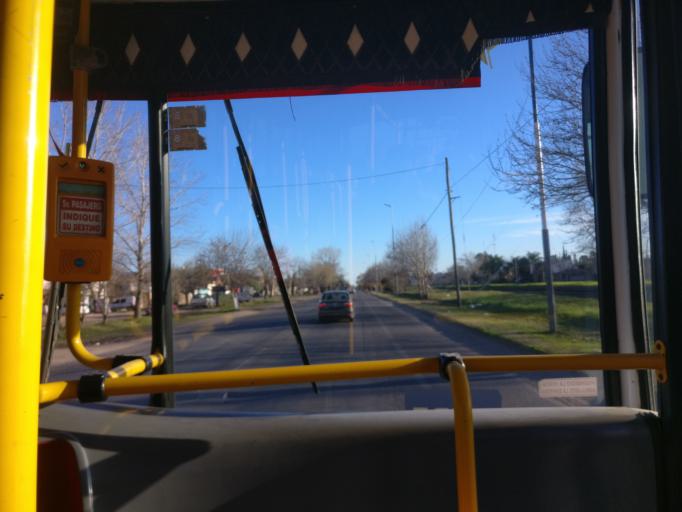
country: AR
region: Buenos Aires
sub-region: Partido de Ezeiza
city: Ezeiza
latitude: -34.9071
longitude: -58.5900
